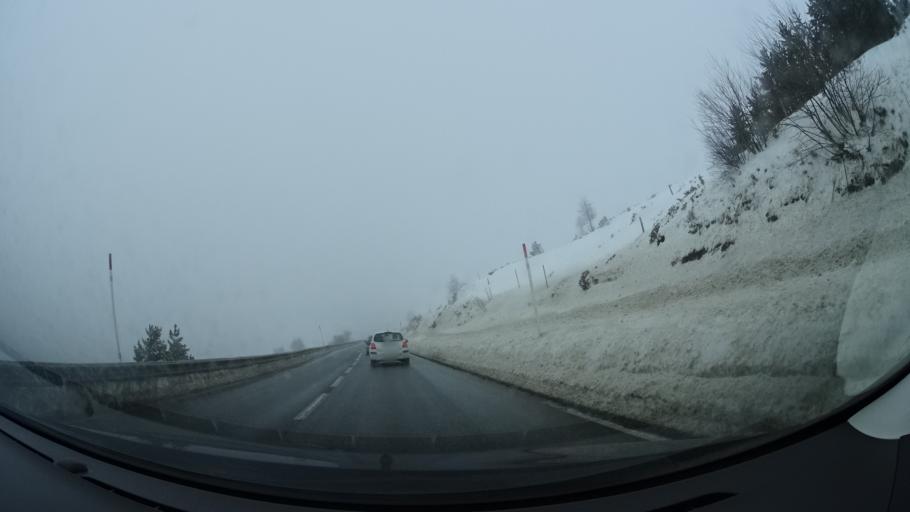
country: AD
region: Encamp
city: Pas de la Casa
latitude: 42.5604
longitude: 1.7609
